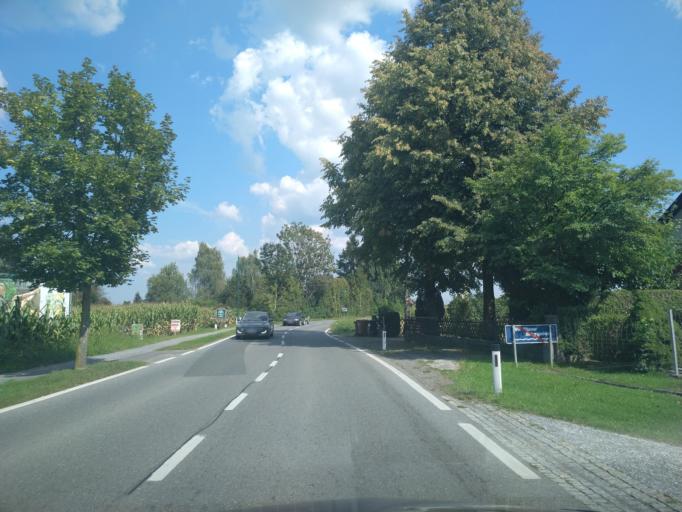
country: AT
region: Styria
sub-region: Politischer Bezirk Leibnitz
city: Gabersdorf
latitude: 46.7641
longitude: 15.5807
